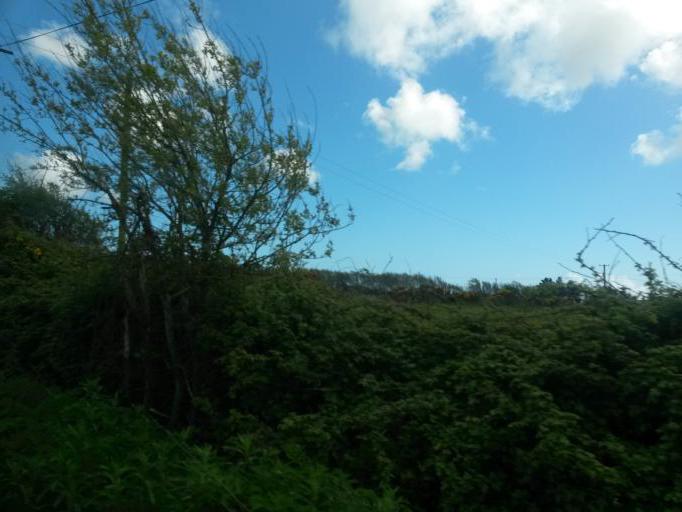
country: IE
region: Munster
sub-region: Waterford
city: Dunmore East
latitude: 52.2099
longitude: -6.9003
